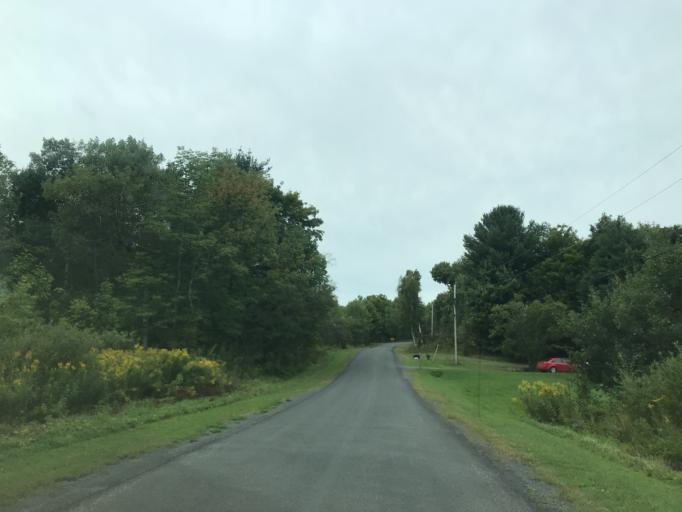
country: US
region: New York
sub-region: Otsego County
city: Worcester
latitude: 42.5317
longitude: -74.6628
